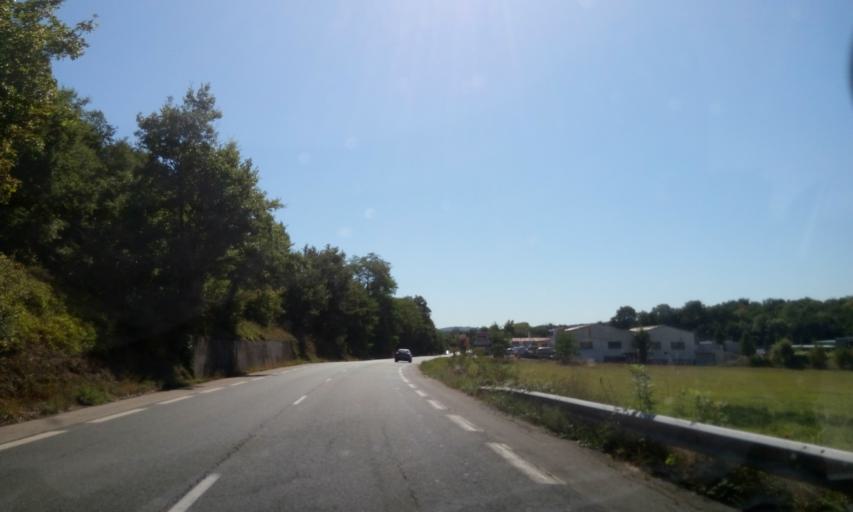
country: FR
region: Rhone-Alpes
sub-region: Departement du Rhone
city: Saint-Verand
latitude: 45.9283
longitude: 4.5565
